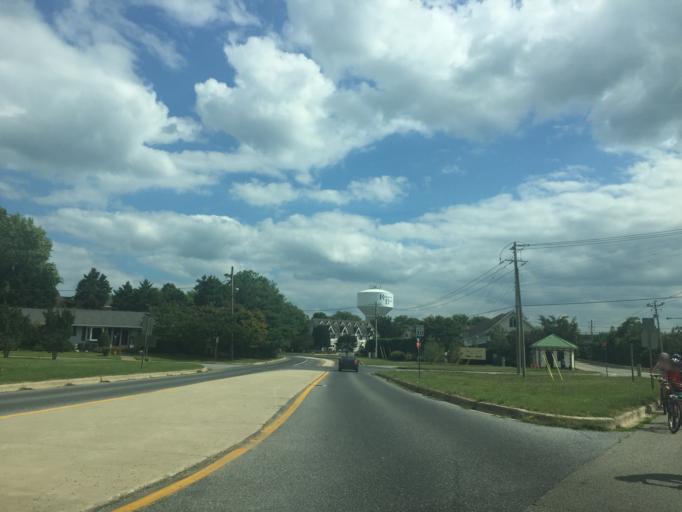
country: US
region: Delaware
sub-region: Sussex County
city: Rehoboth Beach
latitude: 38.7105
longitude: -75.0925
